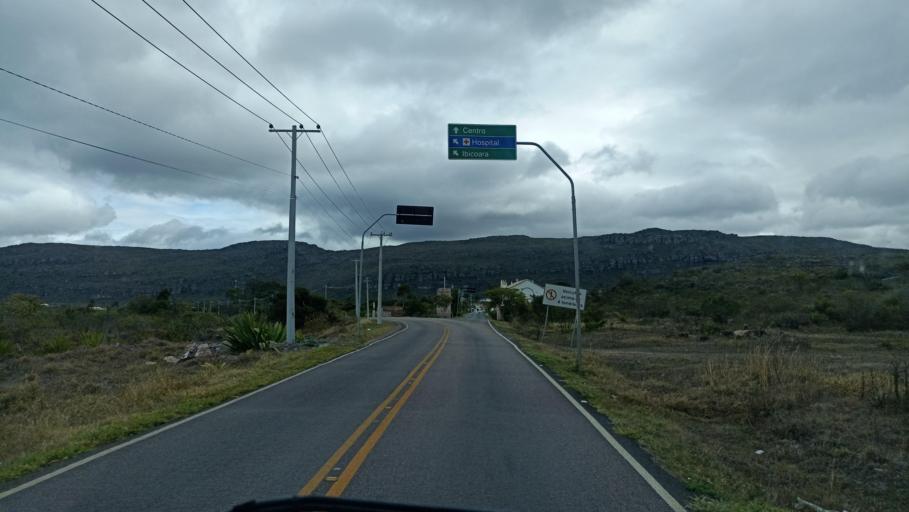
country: BR
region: Bahia
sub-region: Andarai
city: Vera Cruz
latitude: -13.0016
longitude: -41.3651
